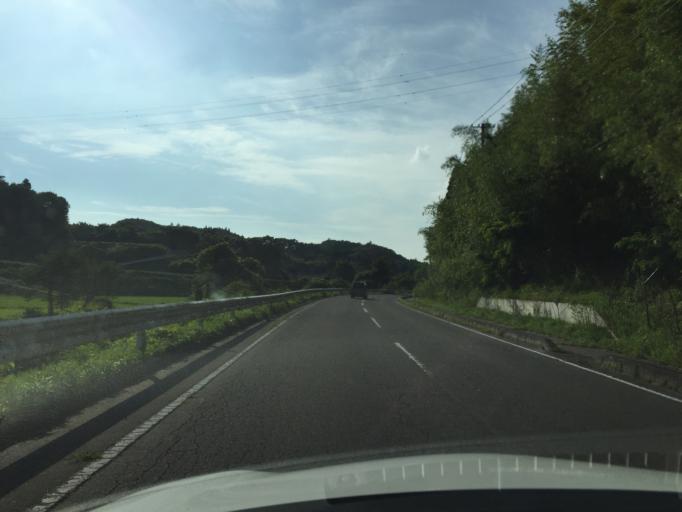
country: JP
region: Fukushima
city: Miharu
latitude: 37.3912
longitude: 140.5056
